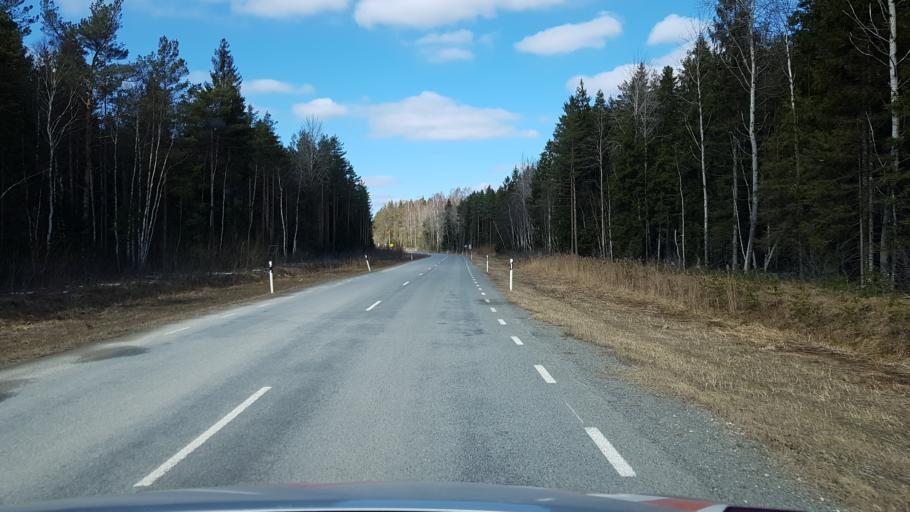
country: EE
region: Laeaene-Virumaa
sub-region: Tapa vald
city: Tapa
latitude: 59.2748
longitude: 25.9149
